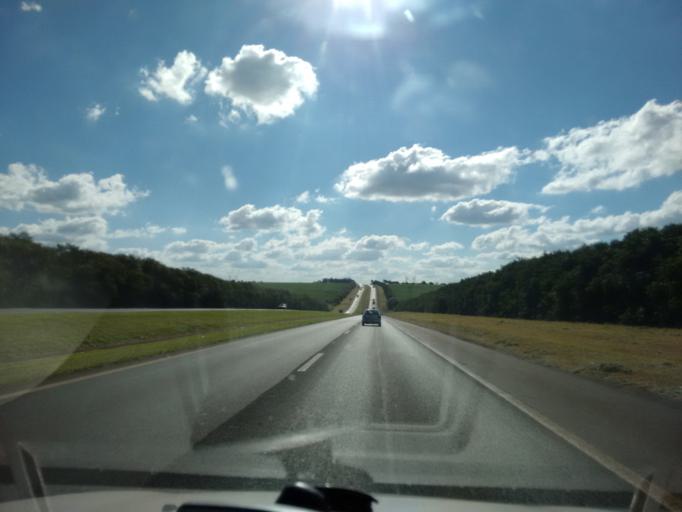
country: BR
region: Sao Paulo
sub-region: Araraquara
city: Araraquara
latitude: -21.8516
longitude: -48.1320
